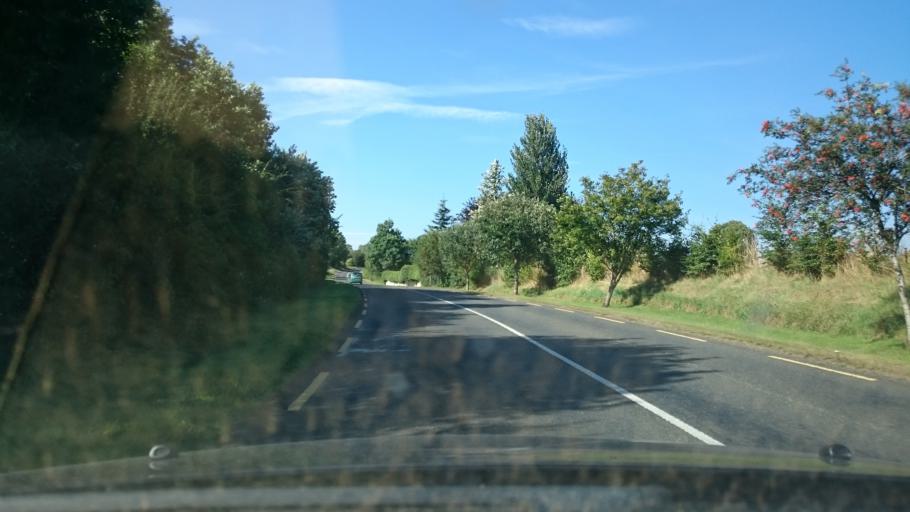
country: IE
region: Leinster
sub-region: Kilkenny
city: Graiguenamanagh
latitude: 52.5481
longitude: -6.9580
